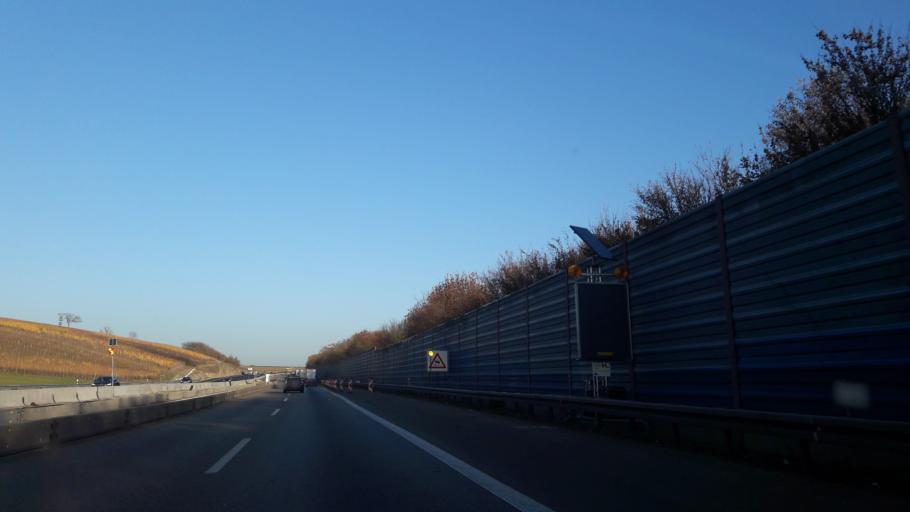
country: DE
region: Baden-Wuerttemberg
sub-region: Karlsruhe Region
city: Rauenberg
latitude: 49.2781
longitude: 8.7050
